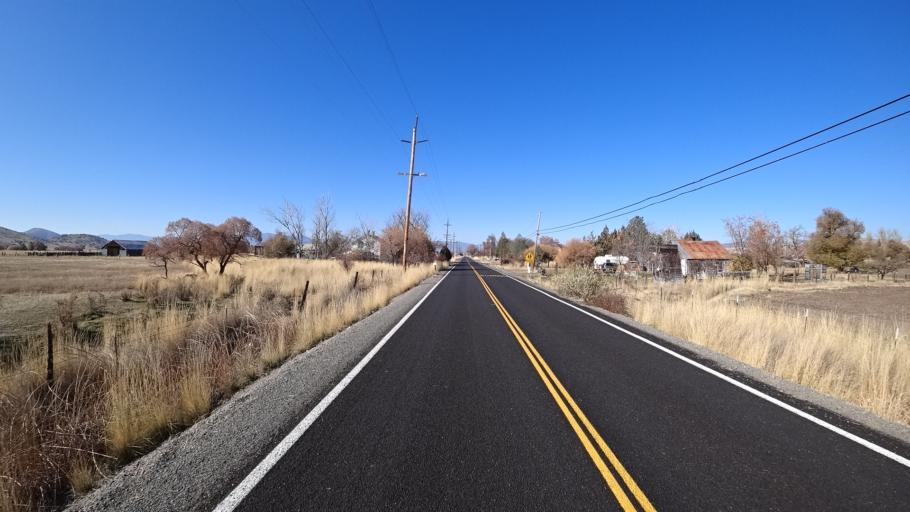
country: US
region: California
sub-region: Siskiyou County
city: Montague
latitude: 41.7114
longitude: -122.3860
